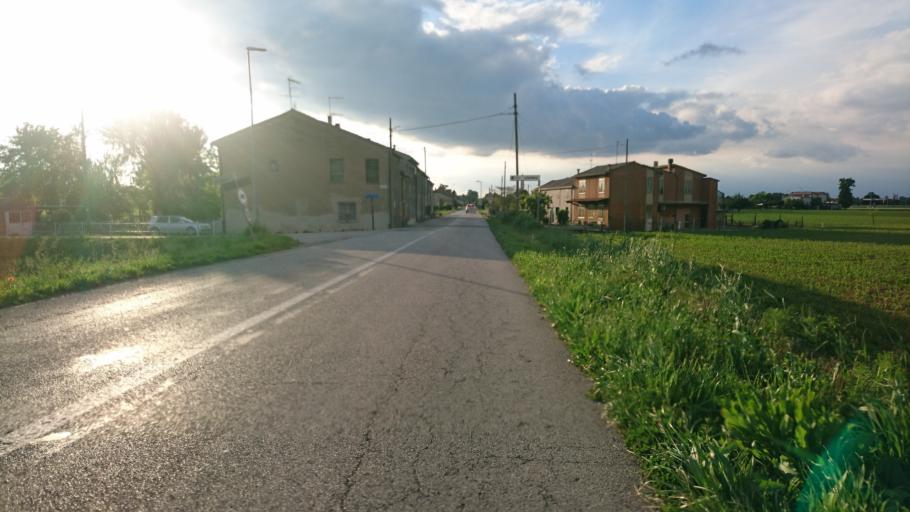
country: IT
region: Veneto
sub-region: Provincia di Rovigo
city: Ceneselli
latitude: 45.0073
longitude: 11.3766
